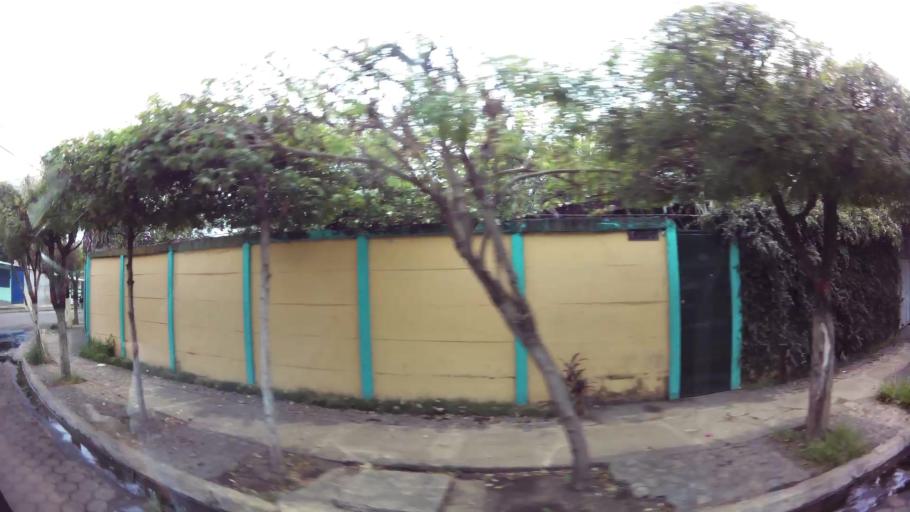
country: NI
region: Chinandega
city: Chinandega
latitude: 12.6253
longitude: -87.1155
